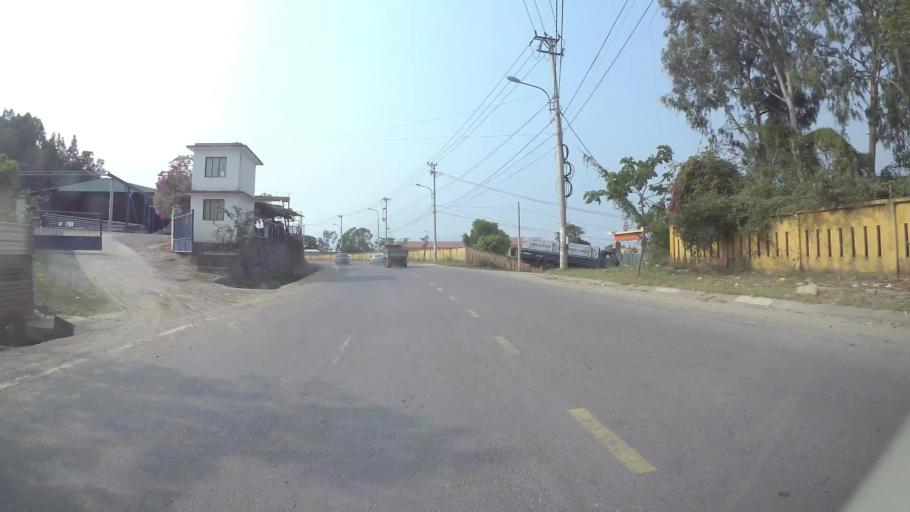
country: VN
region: Da Nang
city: Cam Le
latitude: 16.0380
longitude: 108.1727
